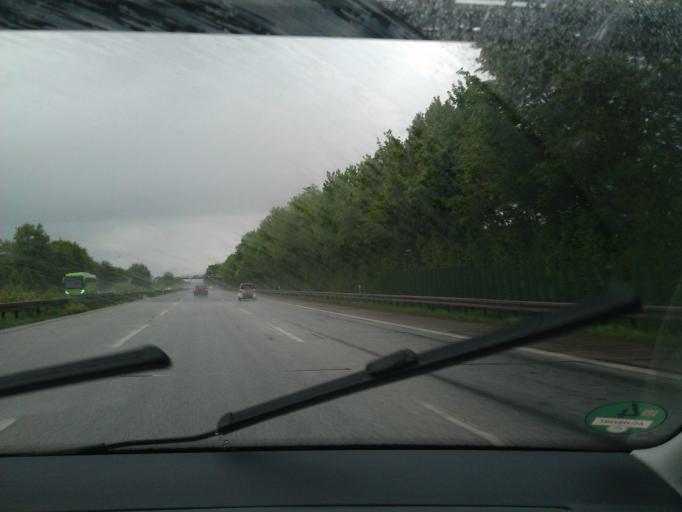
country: DE
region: North Rhine-Westphalia
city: Bornheim
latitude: 50.7787
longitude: 7.0185
